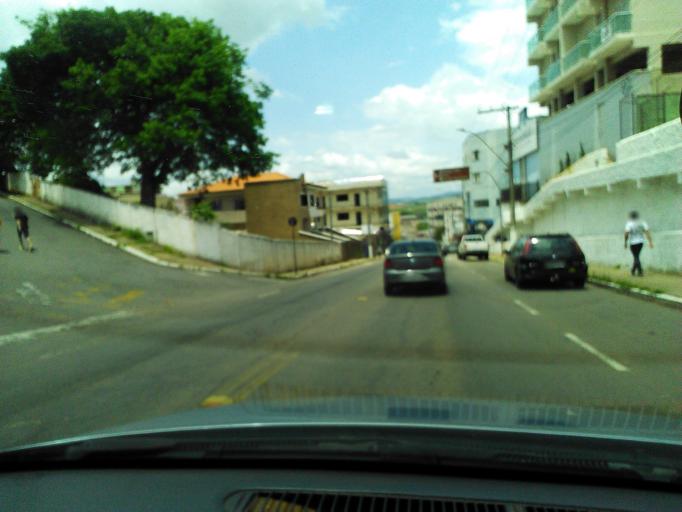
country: BR
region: Minas Gerais
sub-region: Tres Coracoes
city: Tres Coracoes
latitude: -21.6912
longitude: -45.2591
